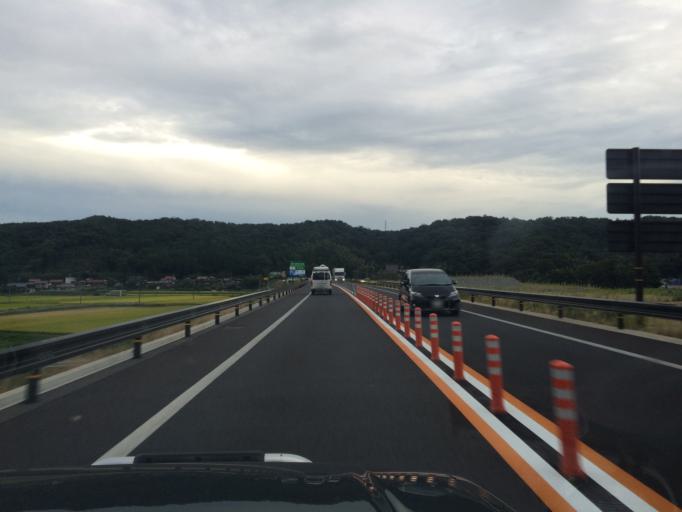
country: JP
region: Tottori
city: Tottori
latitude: 35.4991
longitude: 134.0362
